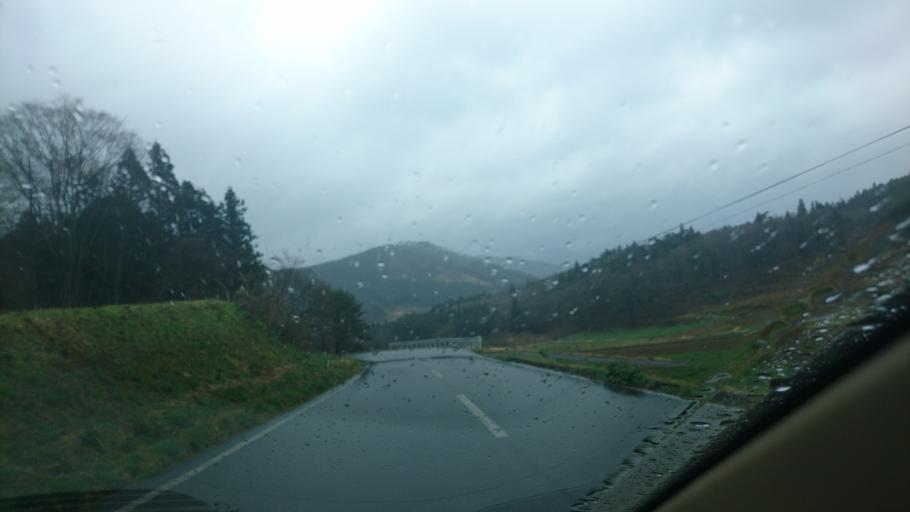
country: JP
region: Iwate
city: Ofunato
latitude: 38.9551
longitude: 141.4566
